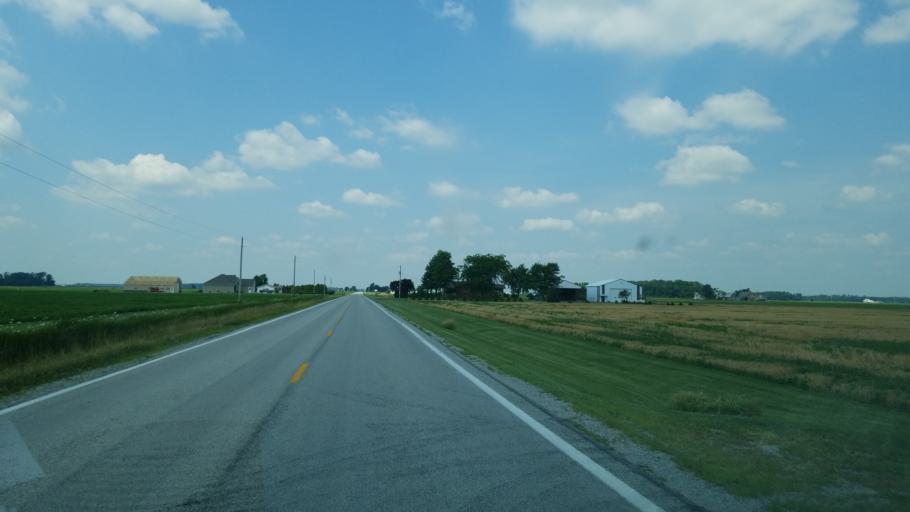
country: US
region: Ohio
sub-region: Henry County
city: Deshler
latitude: 41.2837
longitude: -83.9506
